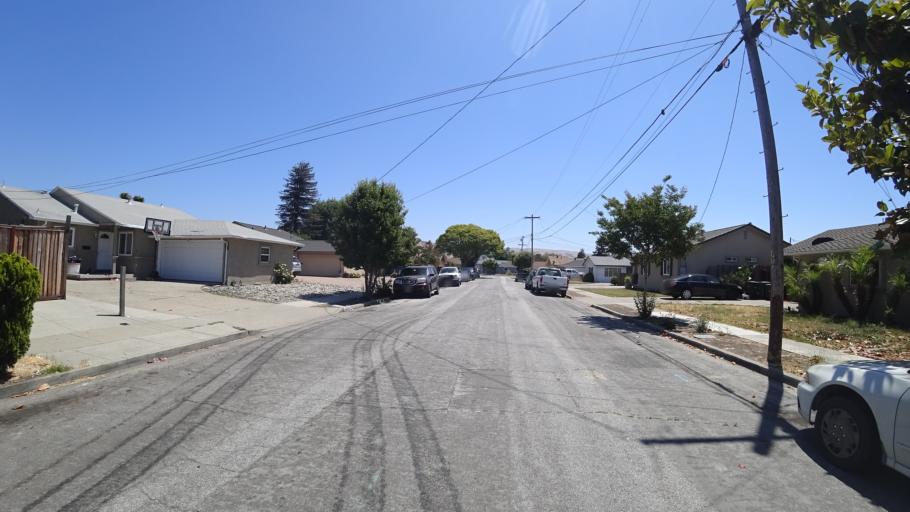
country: US
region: California
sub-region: Alameda County
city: Hayward
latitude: 37.6291
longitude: -122.0737
